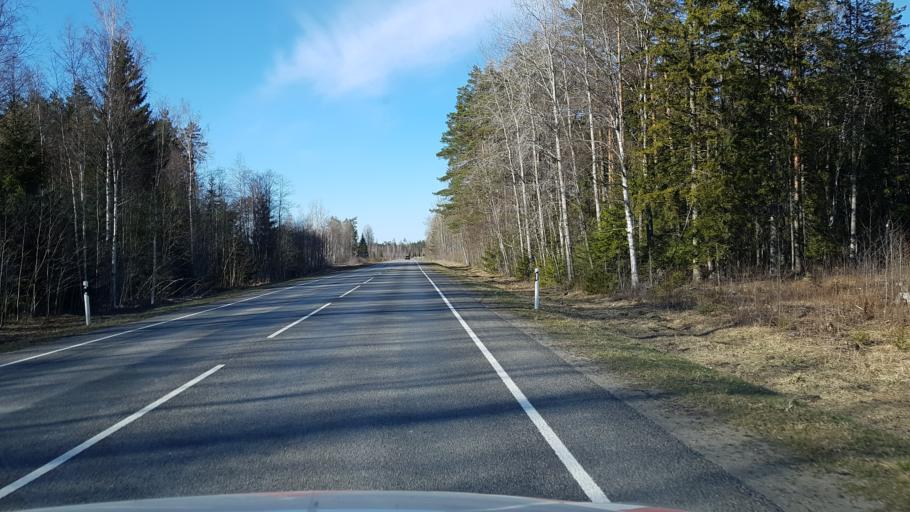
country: EE
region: Jogevamaa
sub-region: Mustvee linn
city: Mustvee
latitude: 59.0124
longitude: 27.2239
